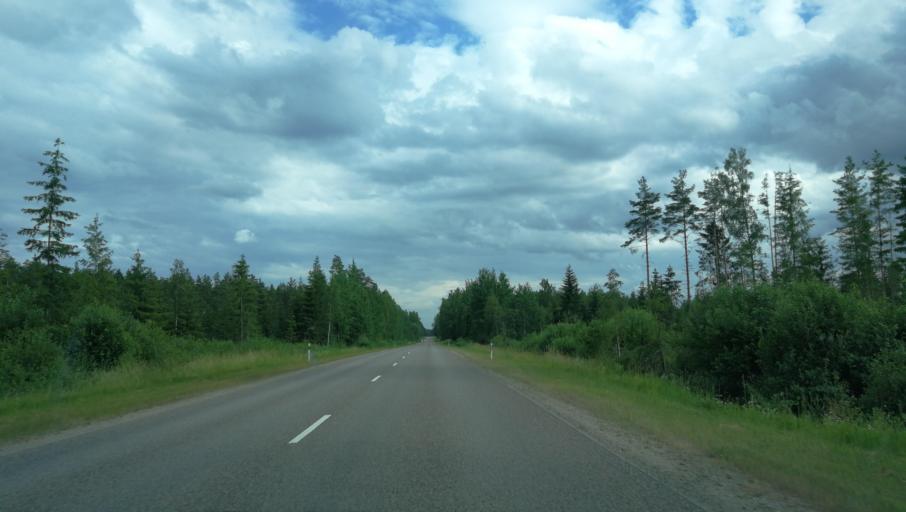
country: LV
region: Naukseni
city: Naukseni
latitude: 57.8201
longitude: 25.3989
